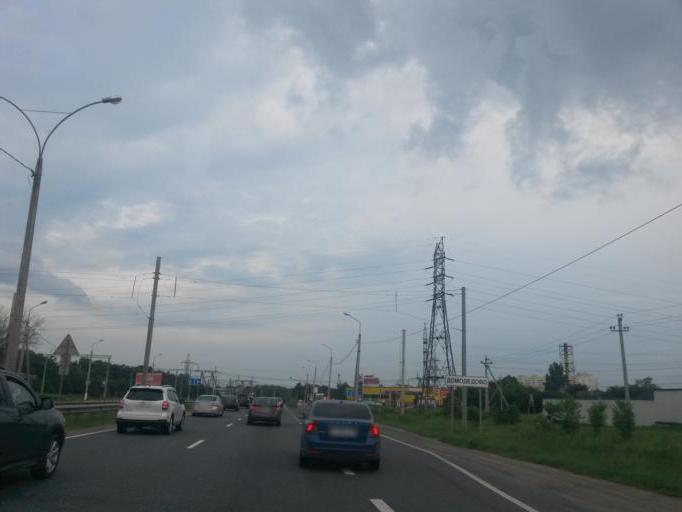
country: RU
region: Moskovskaya
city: Domodedovo
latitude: 55.4624
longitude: 37.7557
